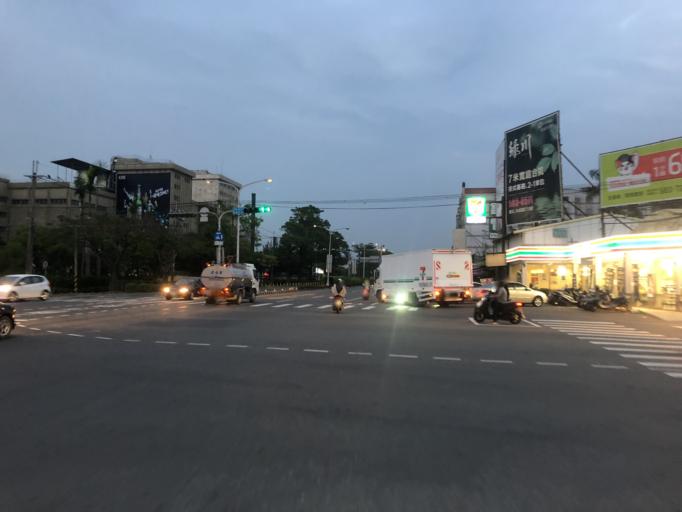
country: TW
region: Taiwan
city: Yujing
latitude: 23.1270
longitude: 120.3188
